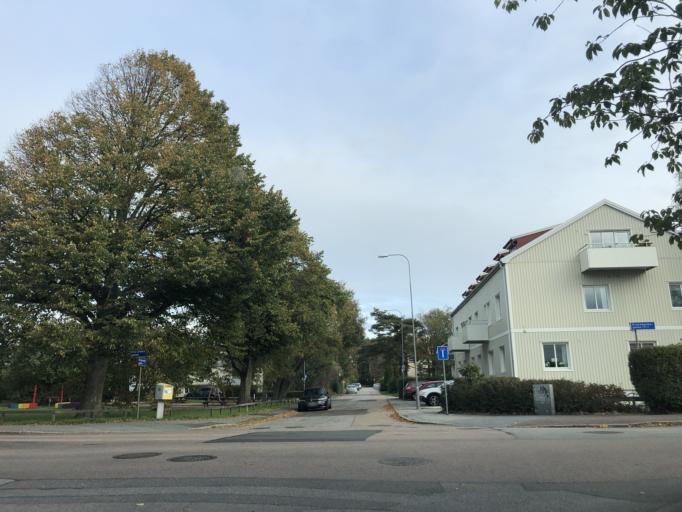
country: SE
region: Vaestra Goetaland
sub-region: Goteborg
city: Majorna
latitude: 57.6760
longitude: 11.8775
